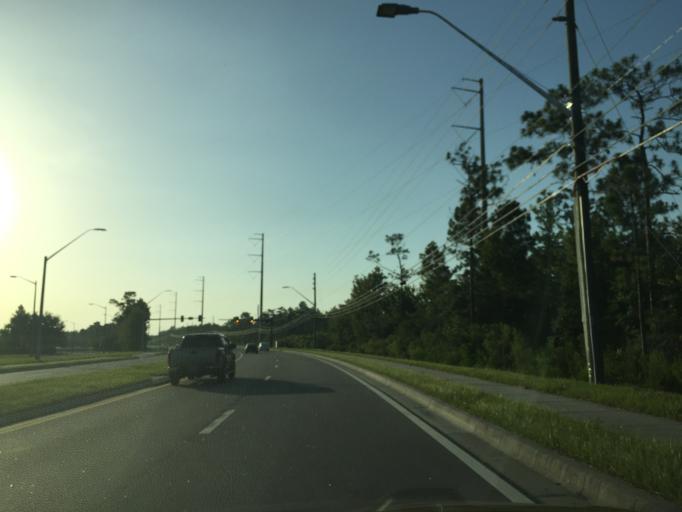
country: US
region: Florida
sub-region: Orange County
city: Alafaya
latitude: 28.5112
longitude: -81.1830
